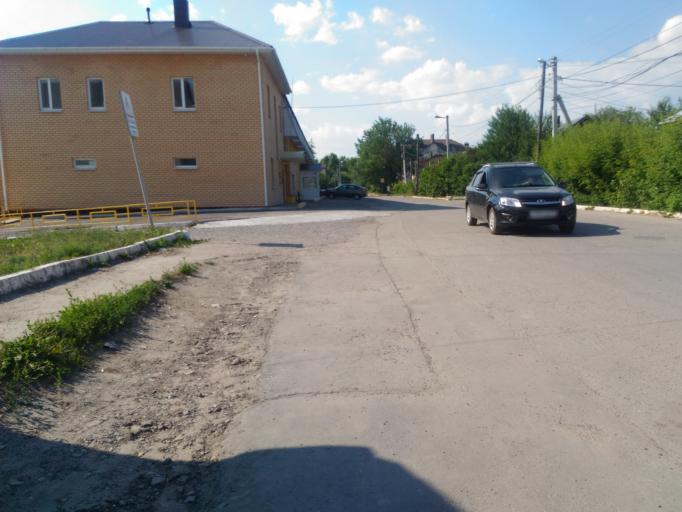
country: RU
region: Ulyanovsk
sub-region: Ulyanovskiy Rayon
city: Ulyanovsk
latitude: 54.3416
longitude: 48.3818
